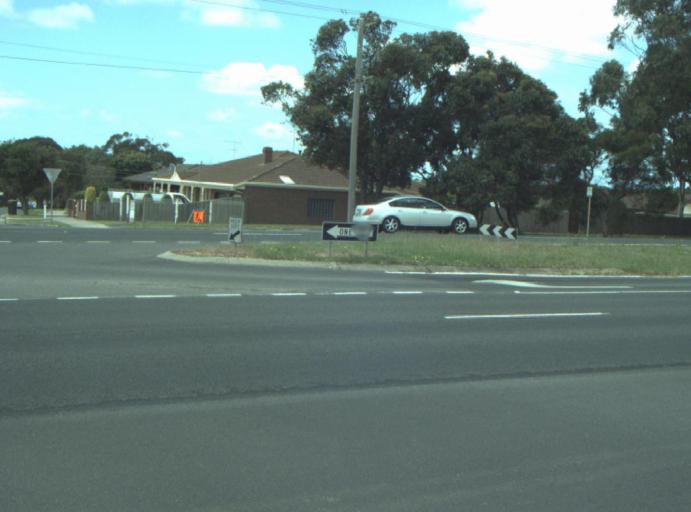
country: AU
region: Victoria
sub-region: Greater Geelong
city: Wandana Heights
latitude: -38.1906
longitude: 144.3259
